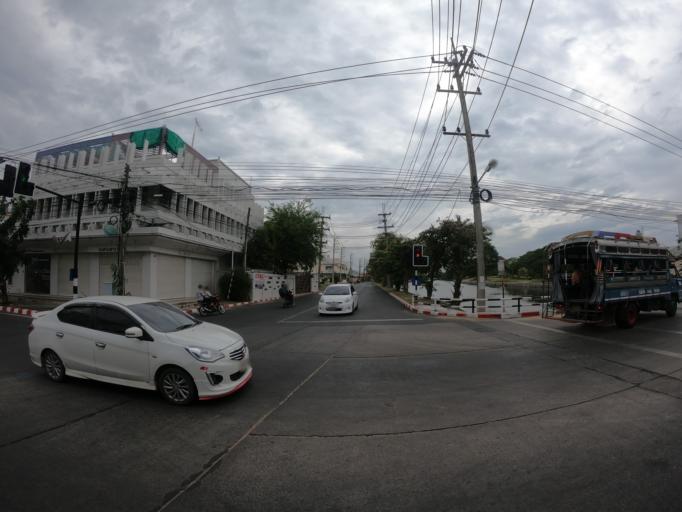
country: TH
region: Roi Et
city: Roi Et
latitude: 16.0613
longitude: 103.6598
